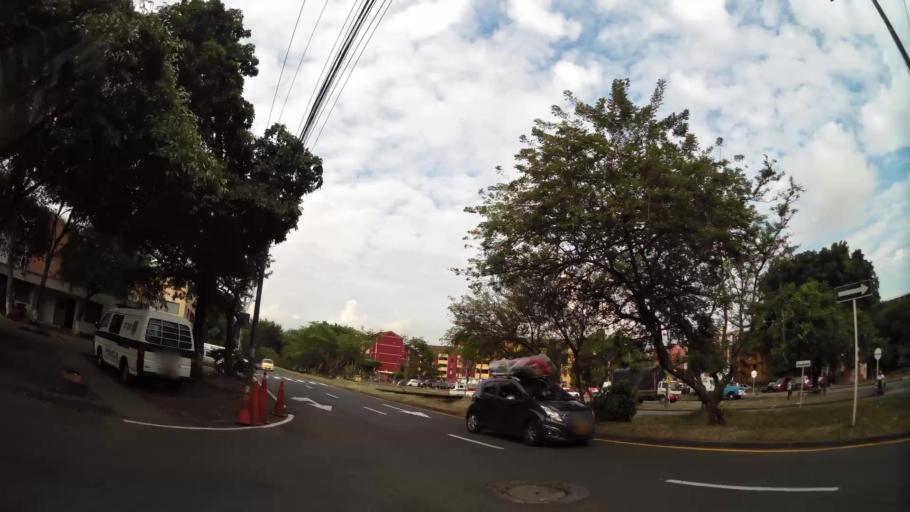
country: CO
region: Valle del Cauca
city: Cali
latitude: 3.4755
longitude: -76.4901
